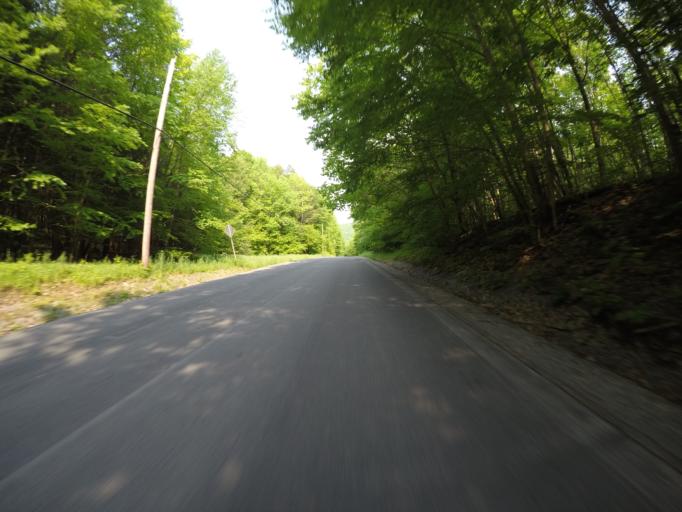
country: US
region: New York
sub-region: Sullivan County
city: Livingston Manor
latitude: 42.1214
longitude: -74.7073
